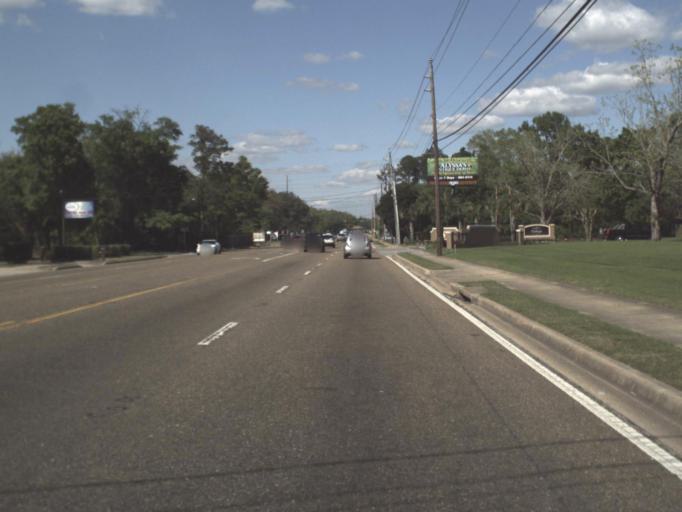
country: US
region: Florida
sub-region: Escambia County
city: Ferry Pass
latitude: 30.5260
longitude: -87.2102
